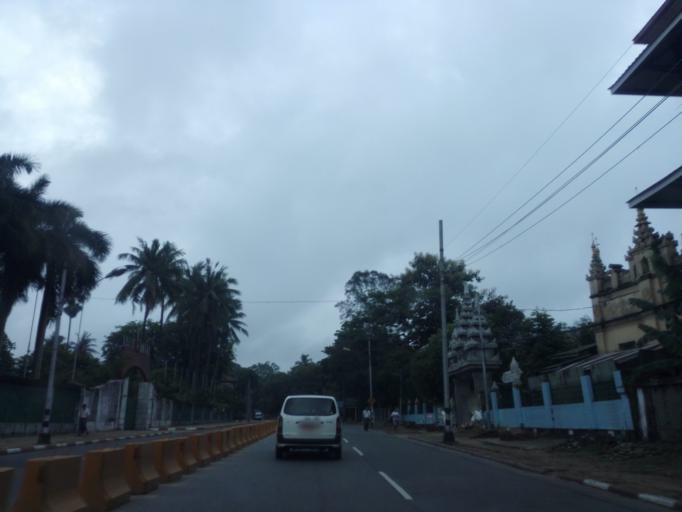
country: MM
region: Yangon
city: Yangon
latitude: 16.7849
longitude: 96.1534
